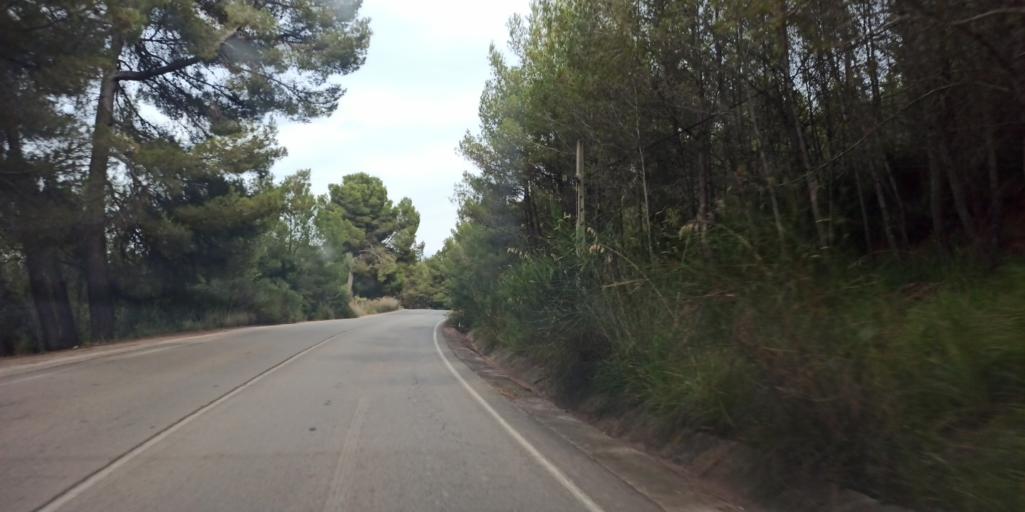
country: ES
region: Catalonia
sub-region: Provincia de Barcelona
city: Castelldefels
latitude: 41.2950
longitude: 1.9714
